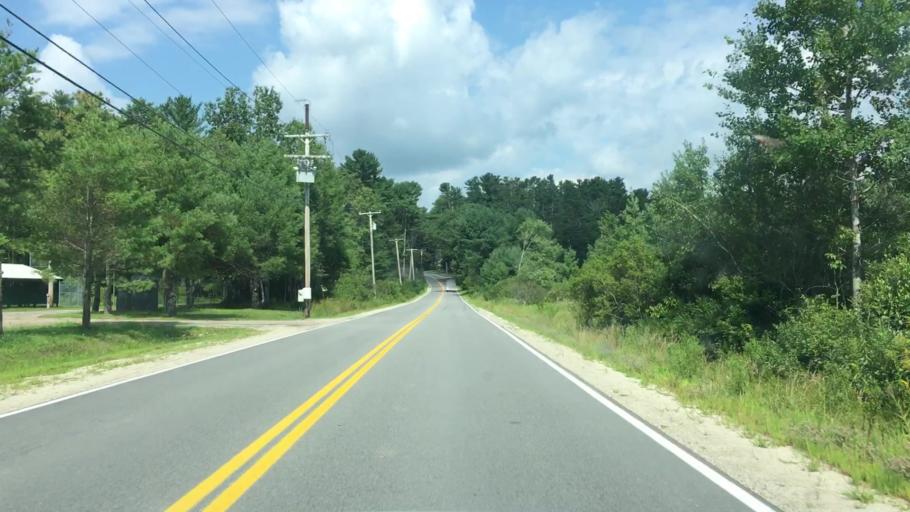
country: US
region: Maine
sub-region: Cumberland County
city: Raymond
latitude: 43.9003
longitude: -70.4575
